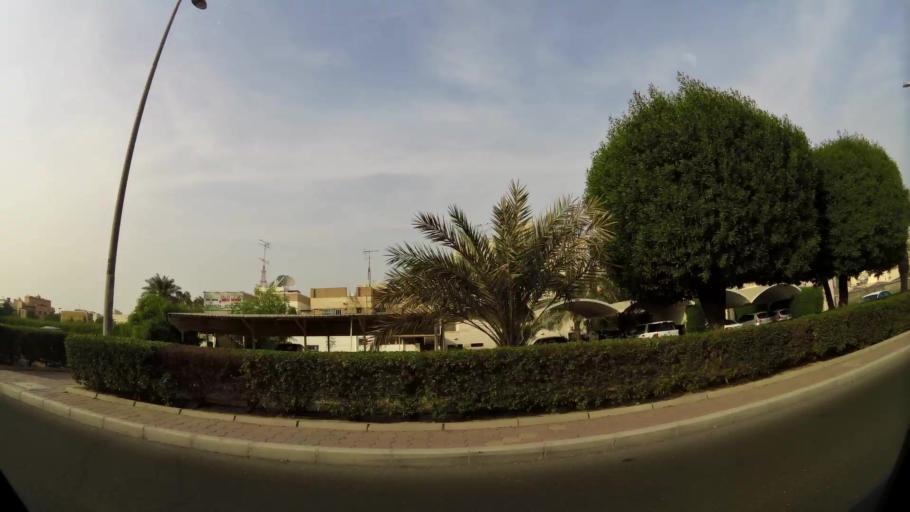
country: KW
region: Mubarak al Kabir
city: Sabah as Salim
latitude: 29.2568
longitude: 48.0507
